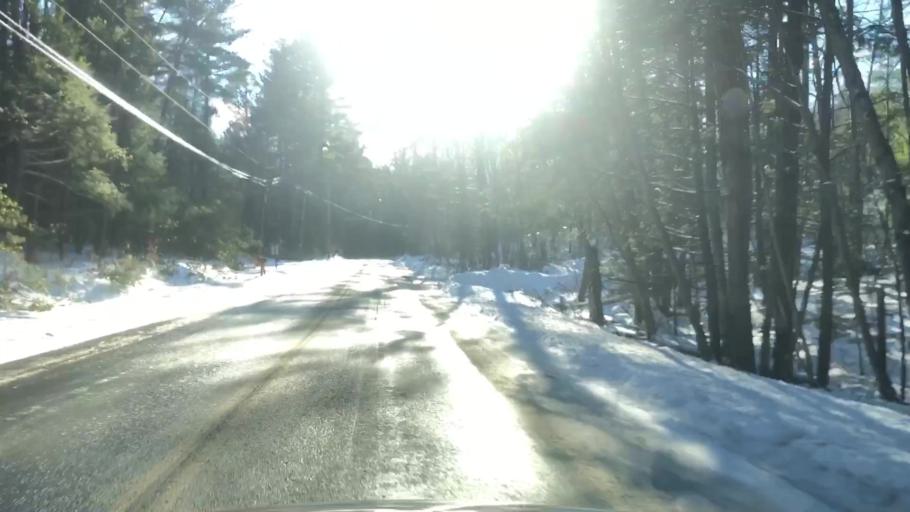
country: US
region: New Hampshire
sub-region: Hillsborough County
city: Wilton
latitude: 42.8298
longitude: -71.7083
